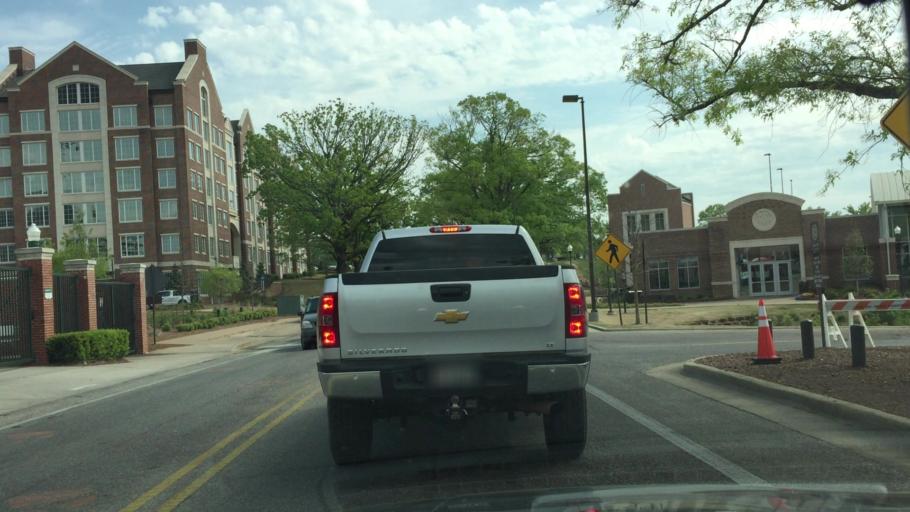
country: US
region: Alabama
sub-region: Lee County
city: Auburn
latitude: 32.5995
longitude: -85.4905
